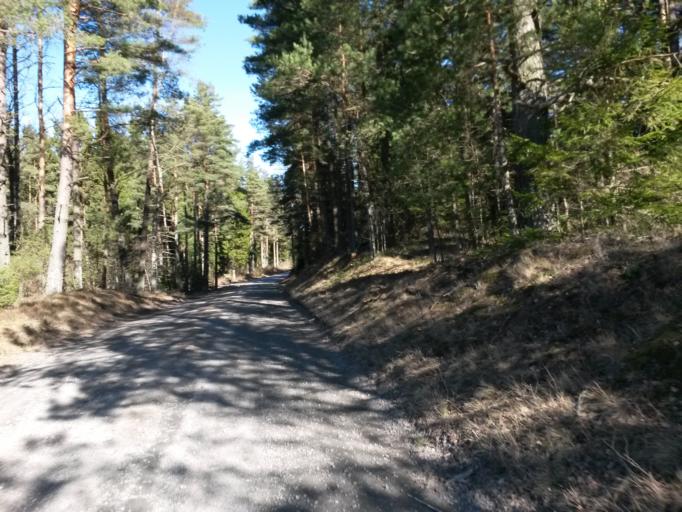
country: SE
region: Vaestra Goetaland
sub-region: Vargarda Kommun
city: Jonstorp
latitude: 57.9841
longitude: 12.7567
